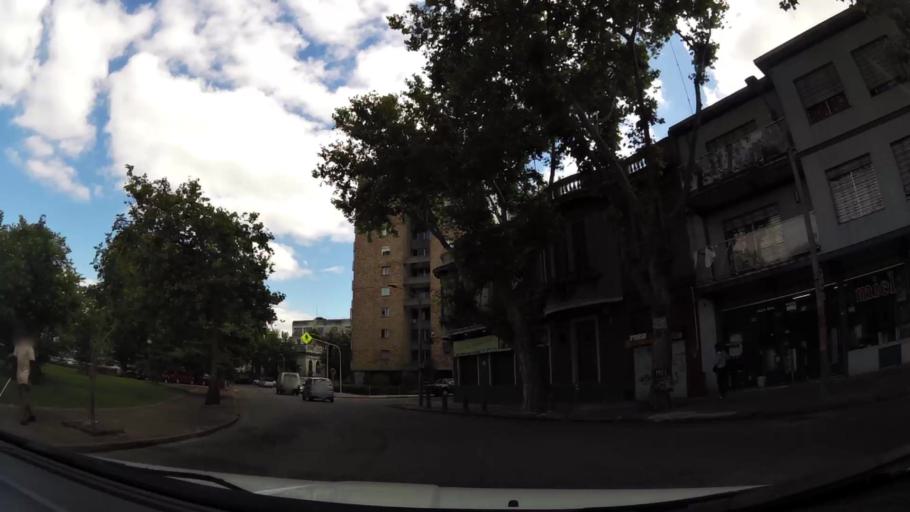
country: UY
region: Montevideo
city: Montevideo
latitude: -34.8899
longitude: -56.1853
